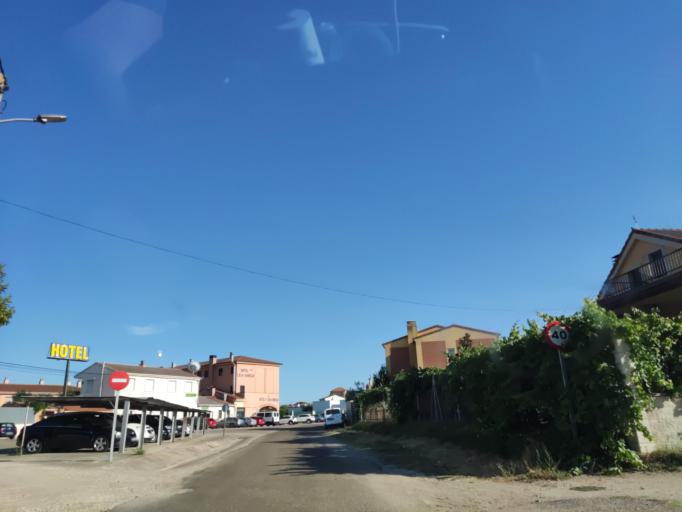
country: ES
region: Castille and Leon
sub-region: Provincia de Zamora
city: Villaralbo
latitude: 41.4953
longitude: -5.6841
